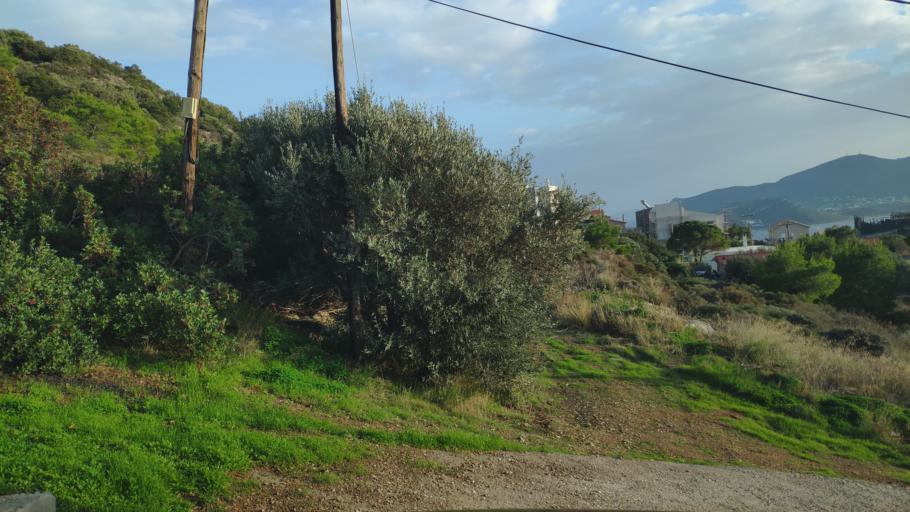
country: GR
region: Attica
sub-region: Nomarchia Anatolikis Attikis
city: Limin Mesoyaias
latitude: 37.9035
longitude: 24.0263
